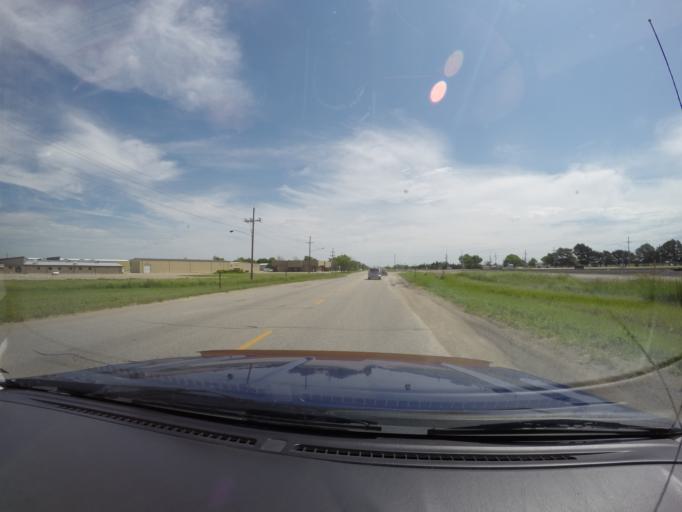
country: US
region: Nebraska
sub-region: Hall County
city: Grand Island
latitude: 40.9022
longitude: -98.3970
